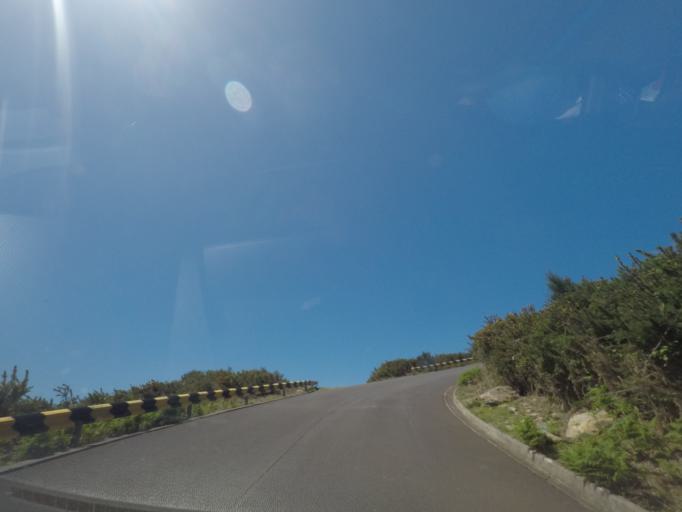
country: PT
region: Madeira
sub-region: Calheta
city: Arco da Calheta
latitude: 32.7436
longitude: -17.1295
